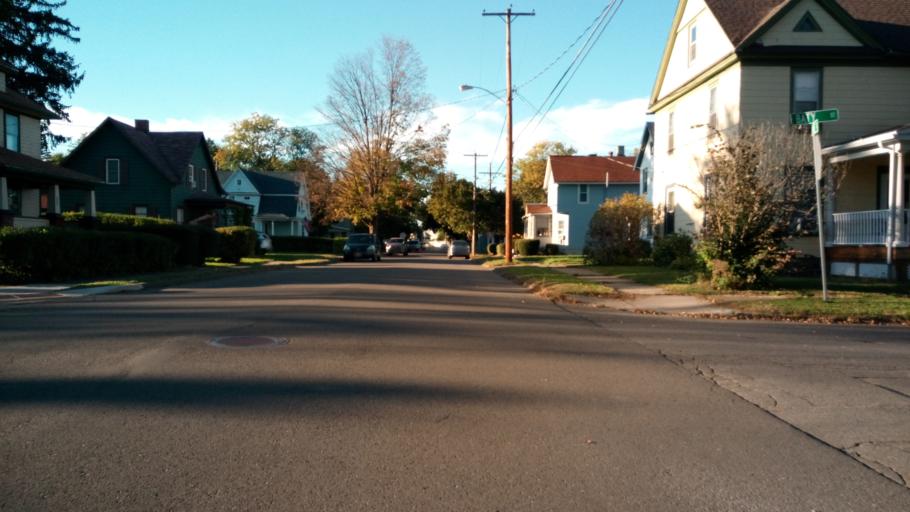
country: US
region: New York
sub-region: Chemung County
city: Elmira
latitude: 42.0722
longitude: -76.8104
